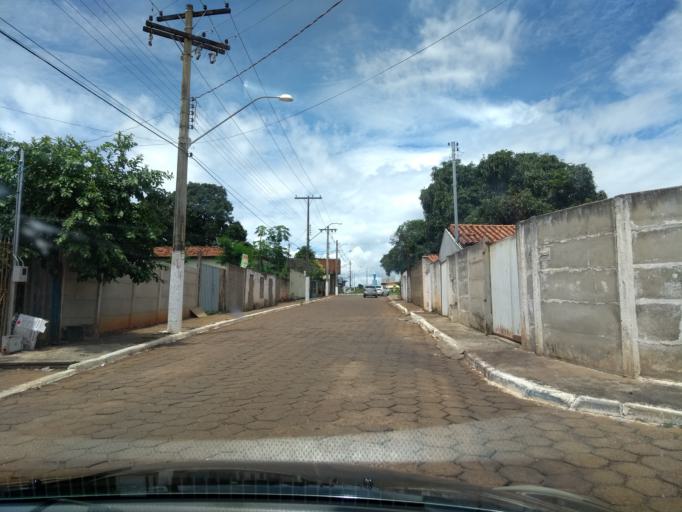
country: BR
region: Goias
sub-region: Luziania
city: Luziania
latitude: -16.2484
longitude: -47.9484
